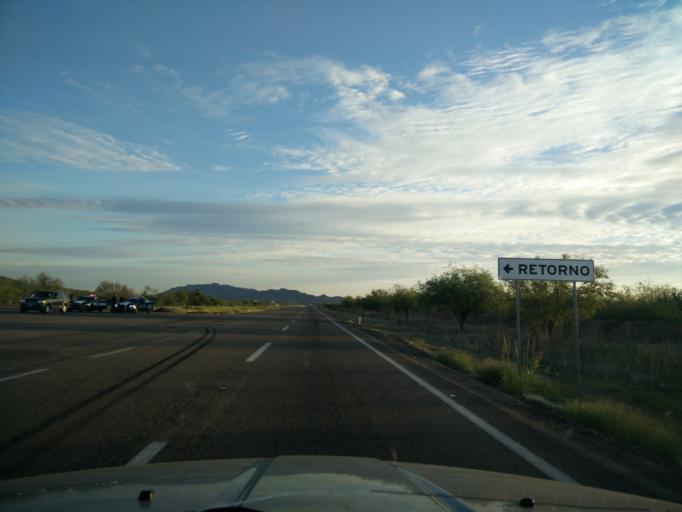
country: MX
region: Sonora
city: Hermosillo
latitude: 28.8784
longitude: -110.9578
